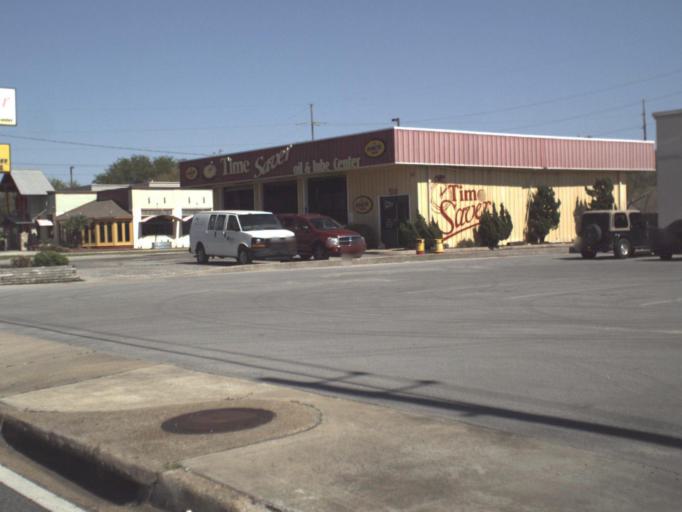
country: US
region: Florida
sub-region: Okaloosa County
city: Mary Esther
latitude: 30.4236
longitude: -86.6487
